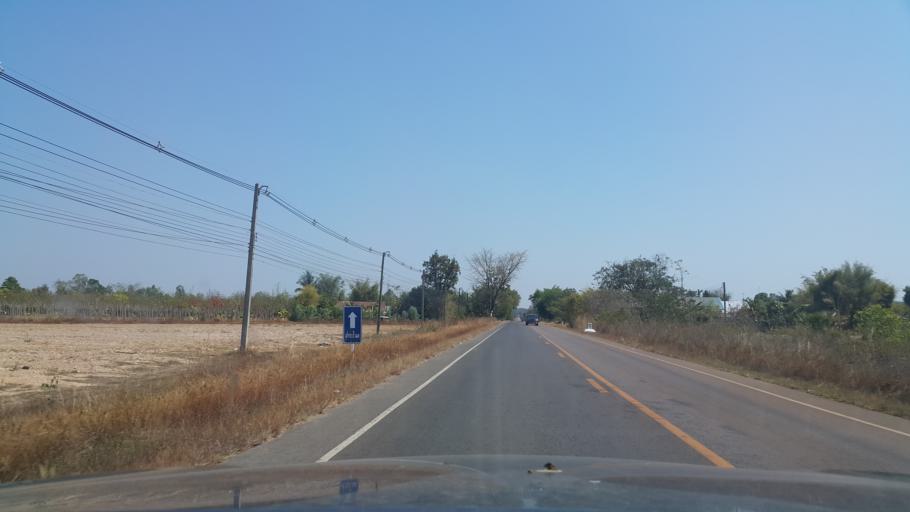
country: TH
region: Changwat Udon Thani
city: Ban Dung
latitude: 17.6087
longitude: 103.2743
